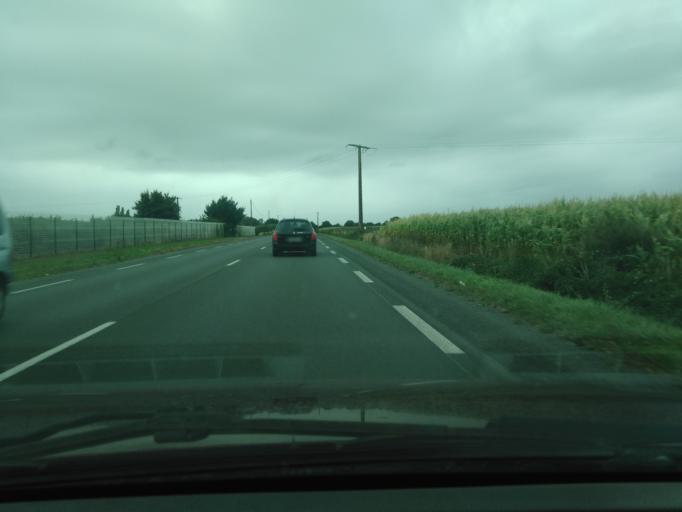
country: FR
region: Pays de la Loire
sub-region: Departement de la Vendee
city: Sainte-Gemme-la-Plaine
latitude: 46.4574
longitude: -1.1057
